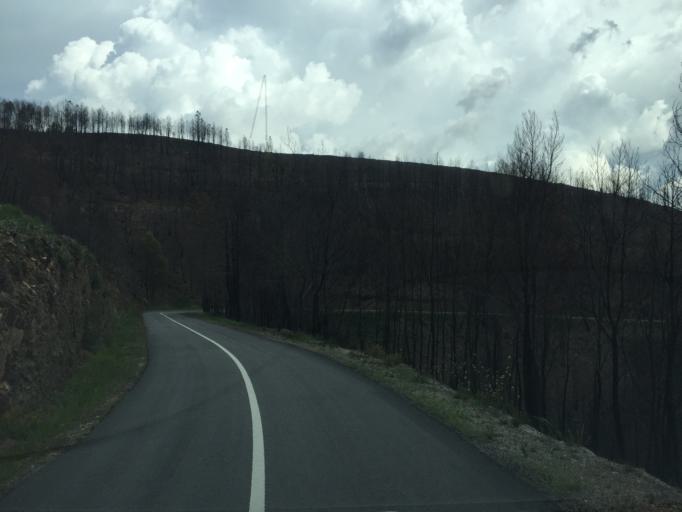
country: PT
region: Coimbra
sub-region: Arganil
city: Arganil
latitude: 40.1829
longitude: -7.9722
